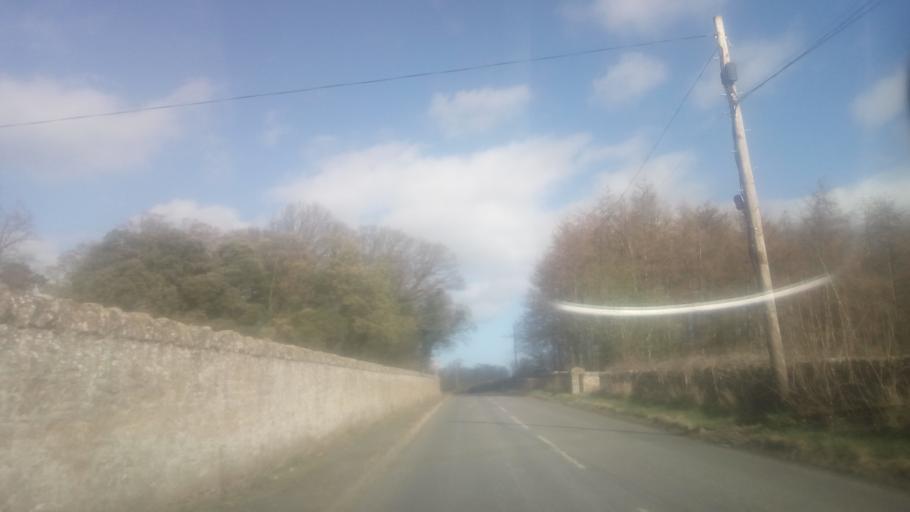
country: GB
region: Scotland
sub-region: Fife
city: Pathhead
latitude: 55.8786
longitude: -2.9612
